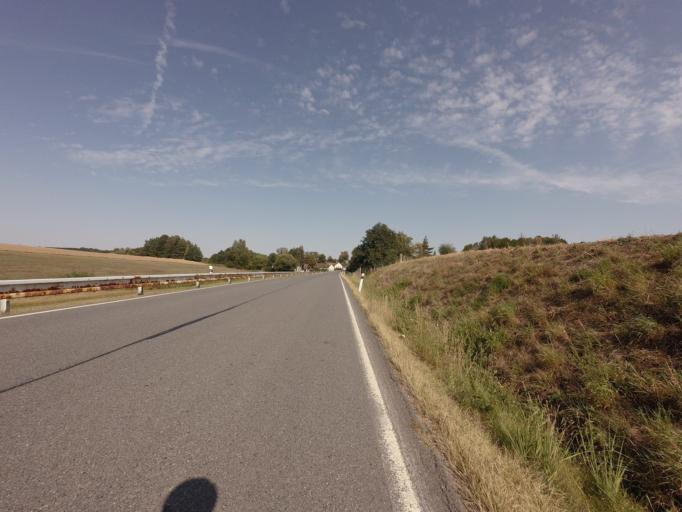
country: CZ
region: Jihocesky
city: Bernartice
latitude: 49.3791
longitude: 14.3683
